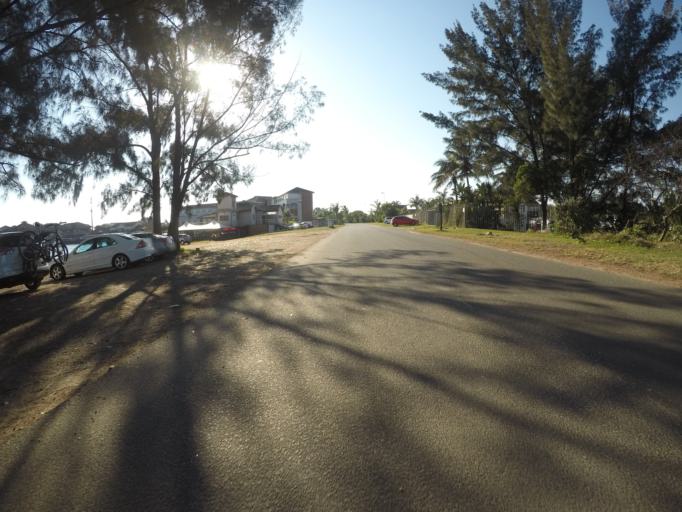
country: ZA
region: KwaZulu-Natal
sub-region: uThungulu District Municipality
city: Richards Bay
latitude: -28.7947
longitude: 32.0817
